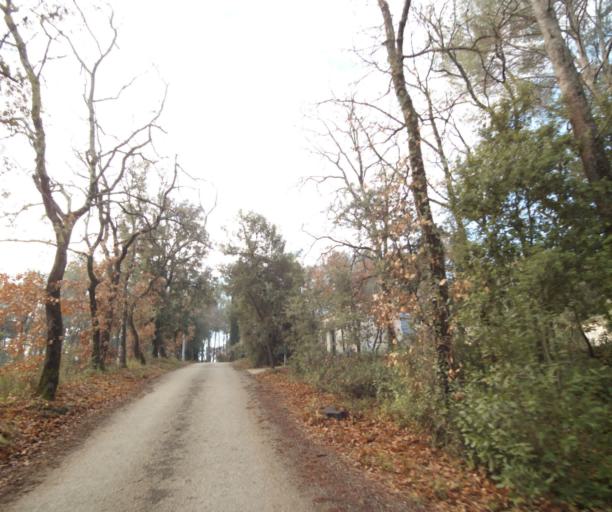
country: FR
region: Provence-Alpes-Cote d'Azur
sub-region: Departement du Var
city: Trans-en-Provence
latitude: 43.4879
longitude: 6.5004
